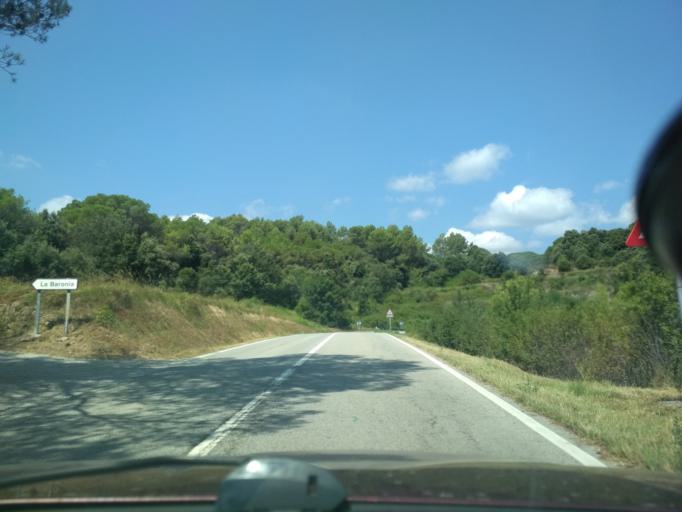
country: ES
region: Catalonia
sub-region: Provincia de Barcelona
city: Sant Feliu de Codines
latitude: 41.7027
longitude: 2.1641
